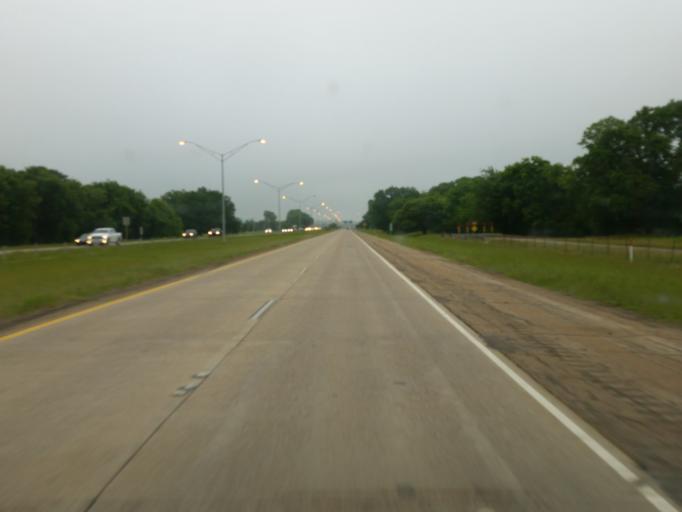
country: US
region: Louisiana
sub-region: Bossier Parish
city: Red Chute
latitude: 32.5352
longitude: -93.6474
